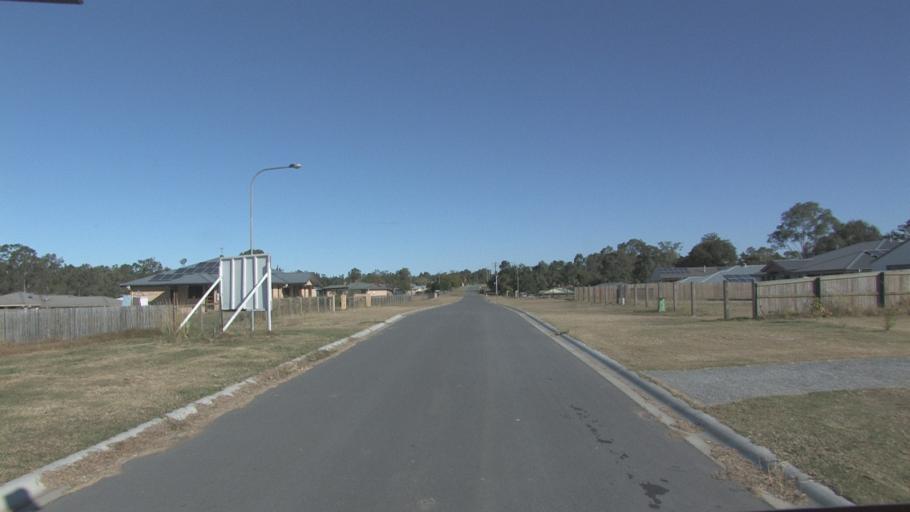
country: AU
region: Queensland
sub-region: Logan
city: North Maclean
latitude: -27.7854
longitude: 153.0255
